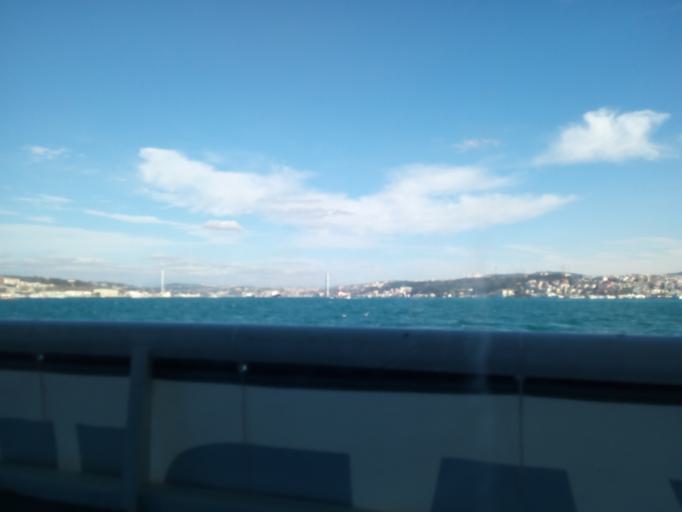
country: TR
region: Istanbul
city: Eminoenue
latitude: 41.0312
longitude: 28.9958
